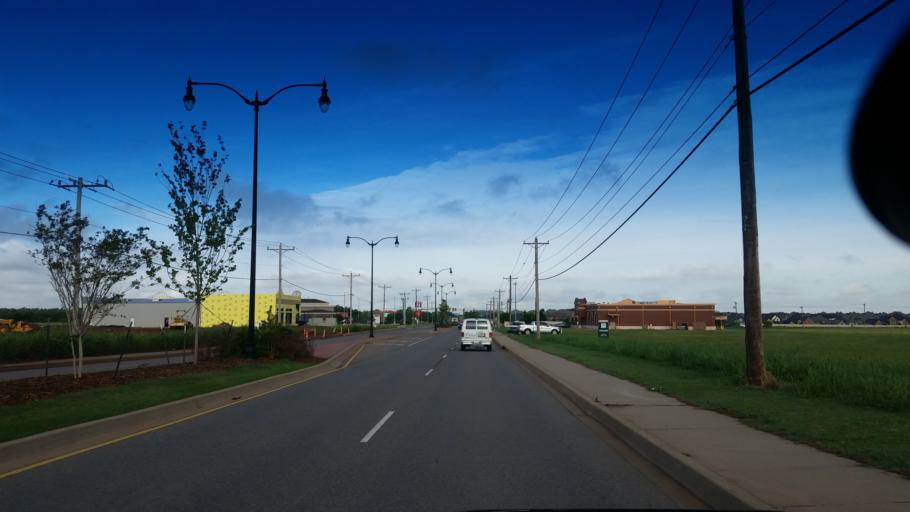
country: US
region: Oklahoma
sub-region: Oklahoma County
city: Edmond
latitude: 35.6238
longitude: -97.5103
